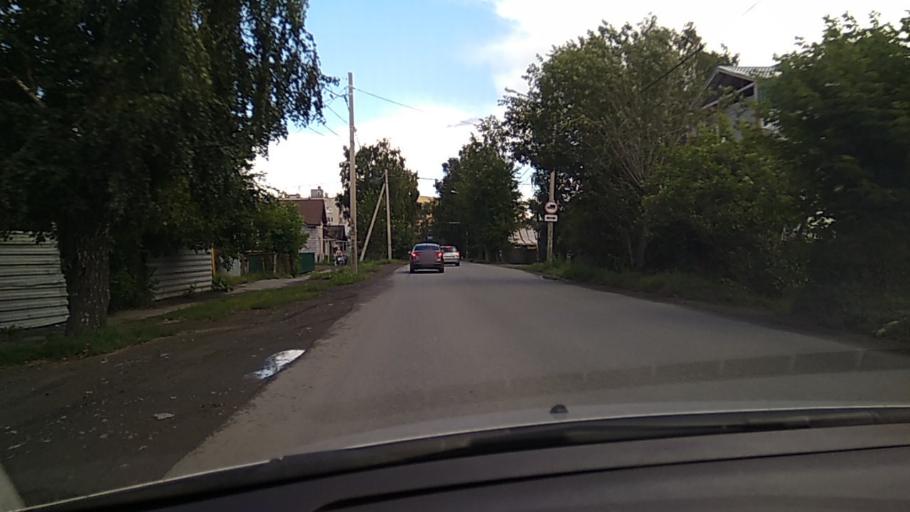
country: RU
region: Sverdlovsk
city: Yekaterinburg
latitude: 56.8812
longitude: 60.5551
